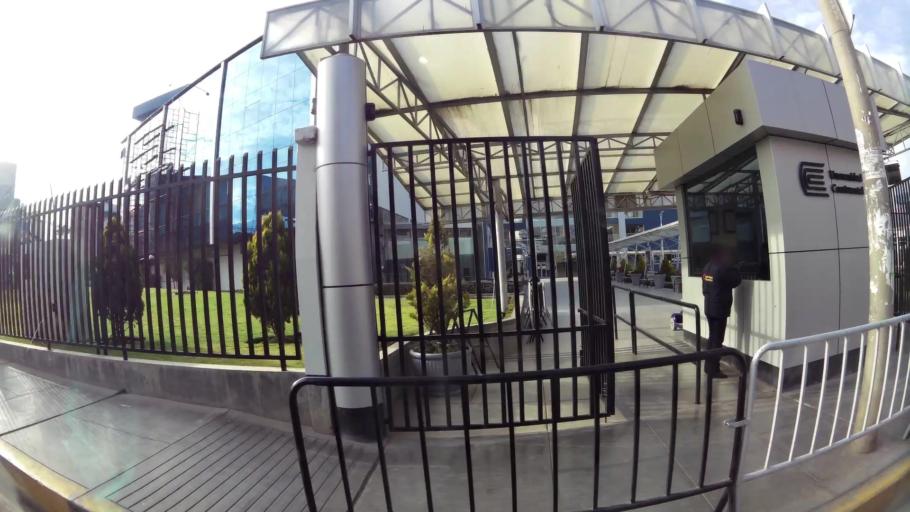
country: PE
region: Junin
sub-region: Provincia de Huancayo
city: Huancayo
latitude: -12.0471
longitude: -75.1991
